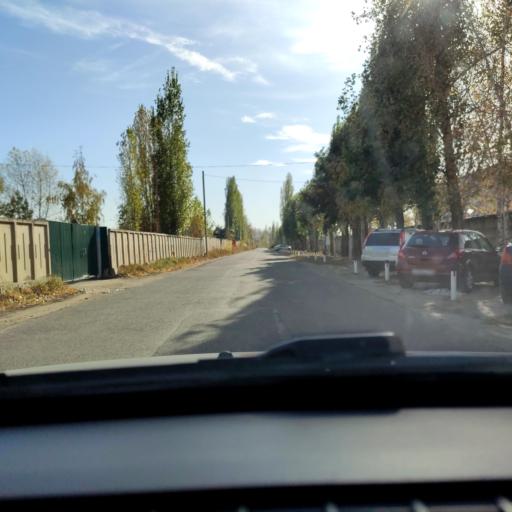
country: RU
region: Voronezj
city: Podgornoye
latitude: 51.8067
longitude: 39.2002
